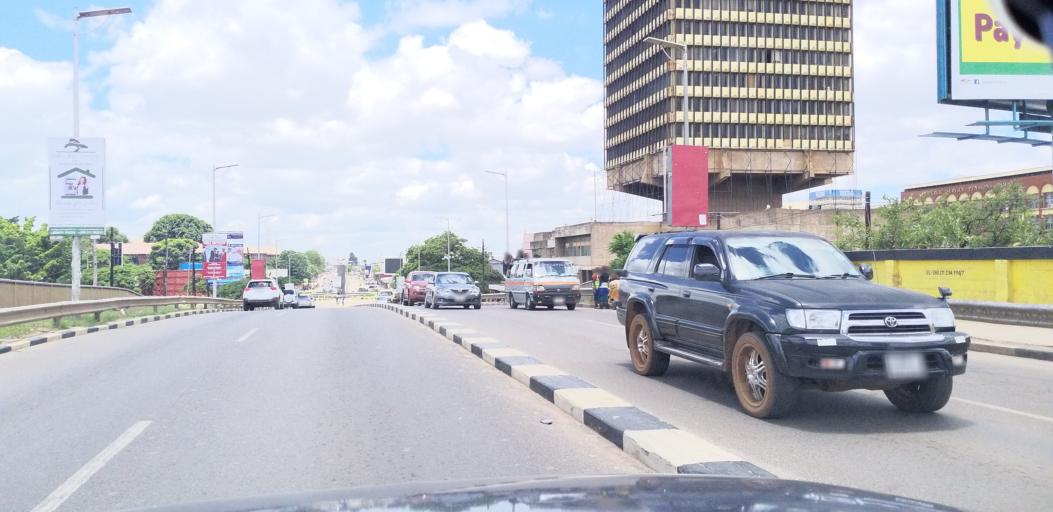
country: ZM
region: Lusaka
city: Lusaka
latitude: -15.4247
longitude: 28.2849
